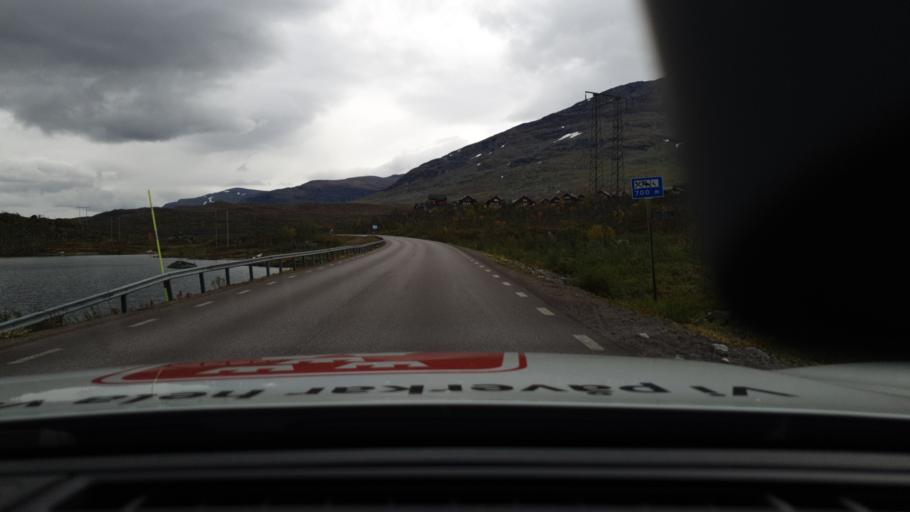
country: NO
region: Troms
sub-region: Lavangen
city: Tennevoll
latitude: 68.4275
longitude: 18.1459
